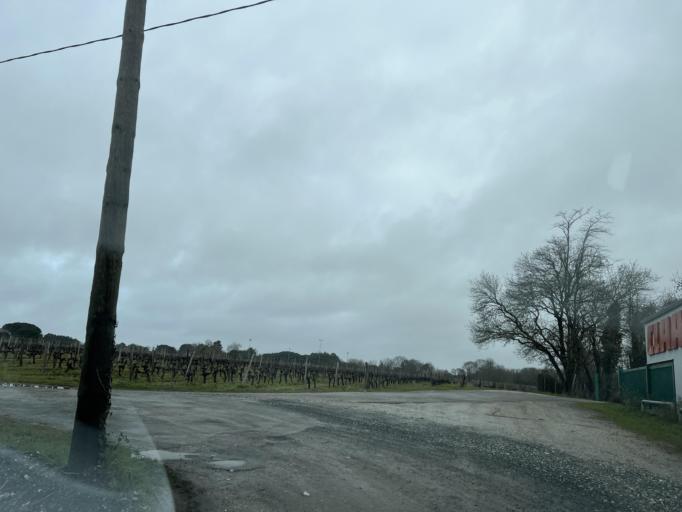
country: FR
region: Aquitaine
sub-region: Departement de la Gironde
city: Gaillan-en-Medoc
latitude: 45.3544
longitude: -0.9821
